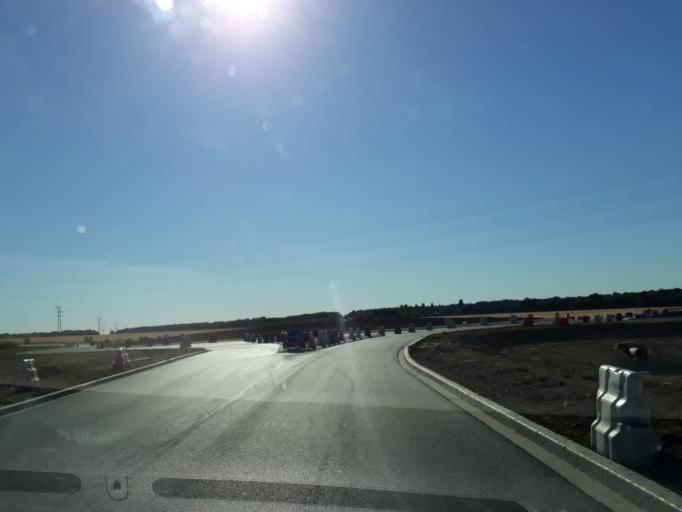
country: FR
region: Centre
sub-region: Departement du Cher
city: Saint-Doulchard
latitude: 47.1242
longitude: 2.3518
